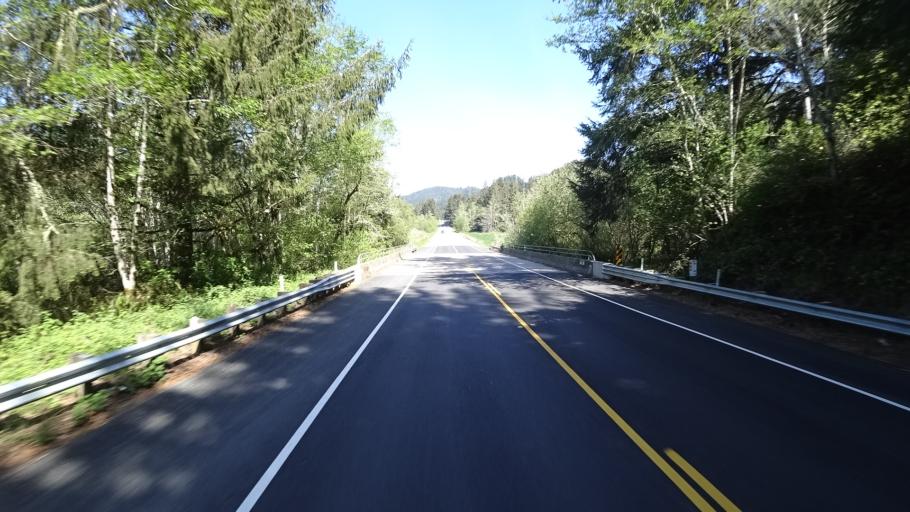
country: US
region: California
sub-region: Del Norte County
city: Bertsch-Oceanview
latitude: 41.5682
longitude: -124.0690
